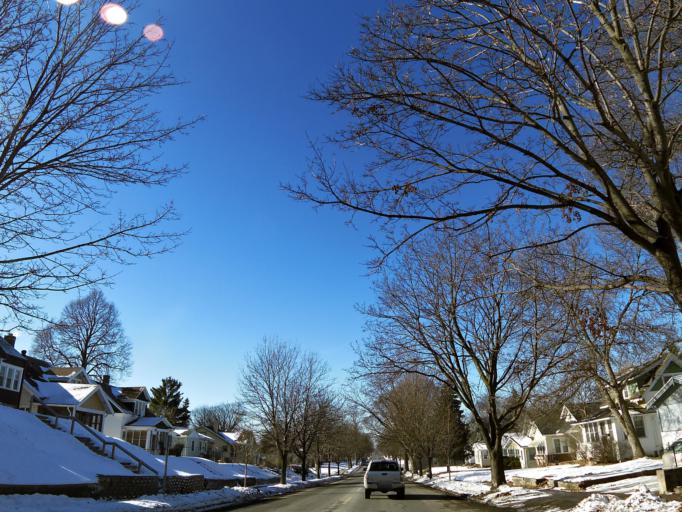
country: US
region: Minnesota
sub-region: Ramsey County
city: Maplewood
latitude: 44.9631
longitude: -93.0289
